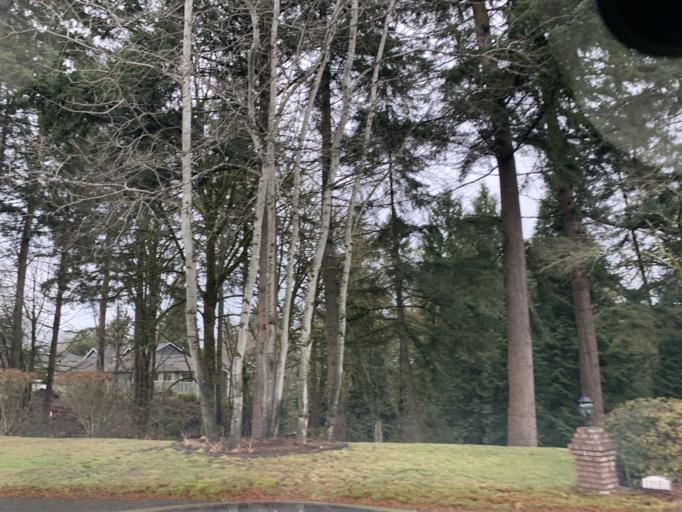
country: US
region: Washington
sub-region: King County
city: Woodinville
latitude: 47.7439
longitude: -122.1692
